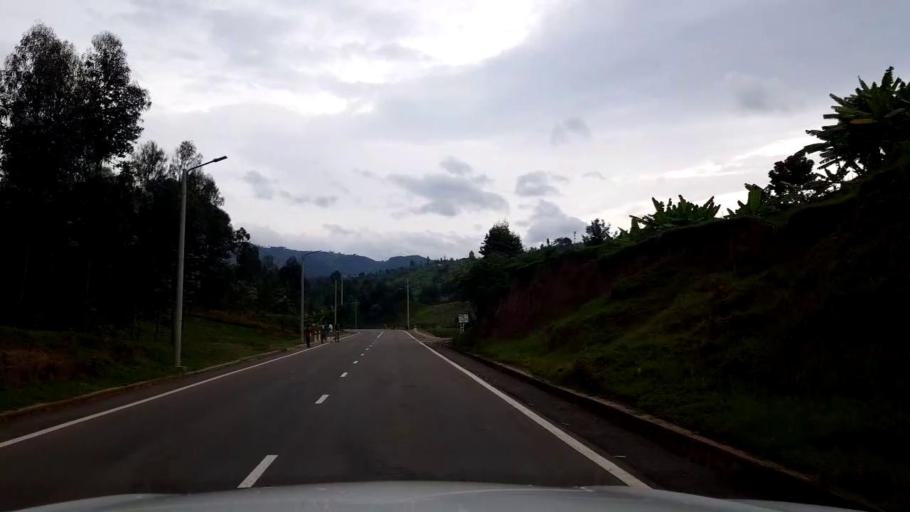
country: RW
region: Western Province
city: Kibuye
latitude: -2.0205
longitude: 29.3898
